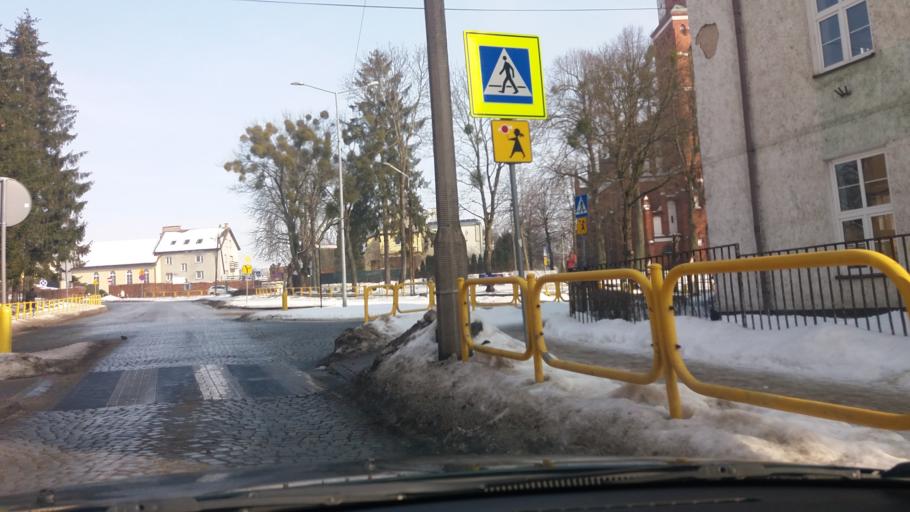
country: PL
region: Warmian-Masurian Voivodeship
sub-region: Powiat szczycienski
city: Szczytno
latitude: 53.5702
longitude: 20.9922
